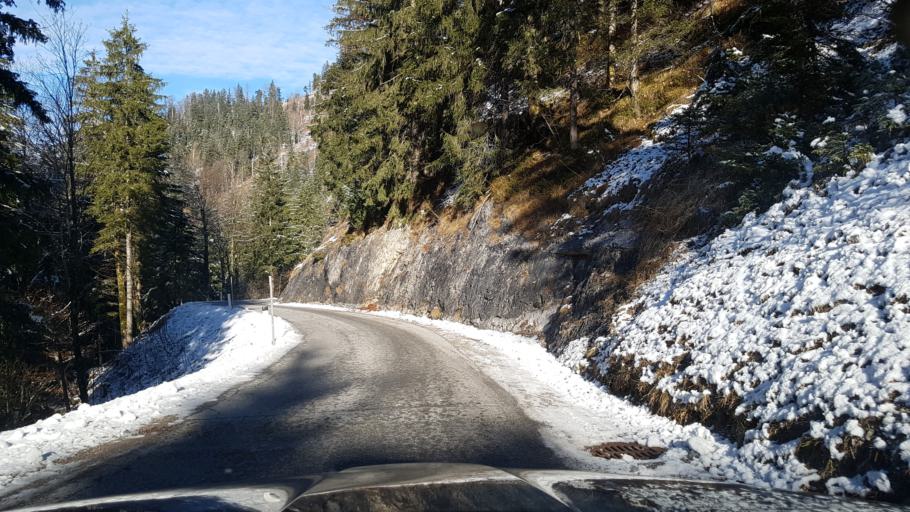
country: AT
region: Salzburg
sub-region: Politischer Bezirk Salzburg-Umgebung
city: Faistenau
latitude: 47.7647
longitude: 13.2282
